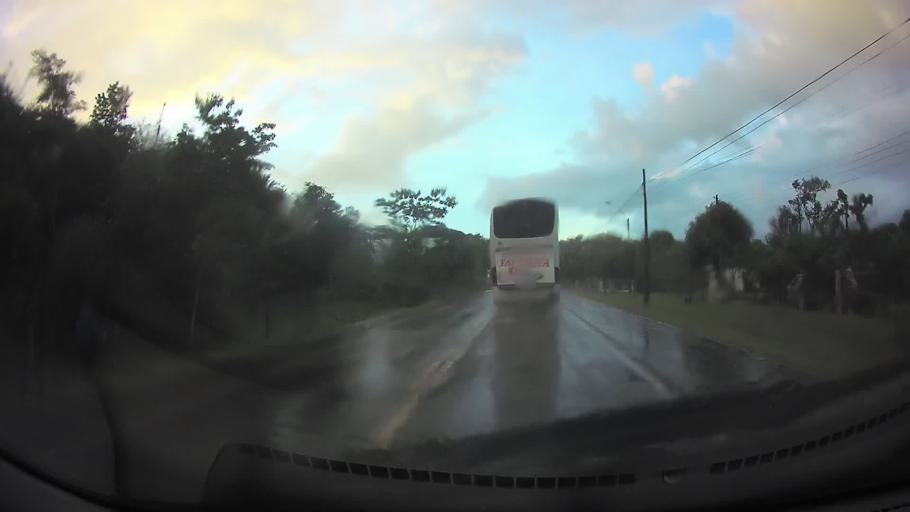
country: PY
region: Paraguari
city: Yaguaron
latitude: -25.5826
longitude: -57.2493
